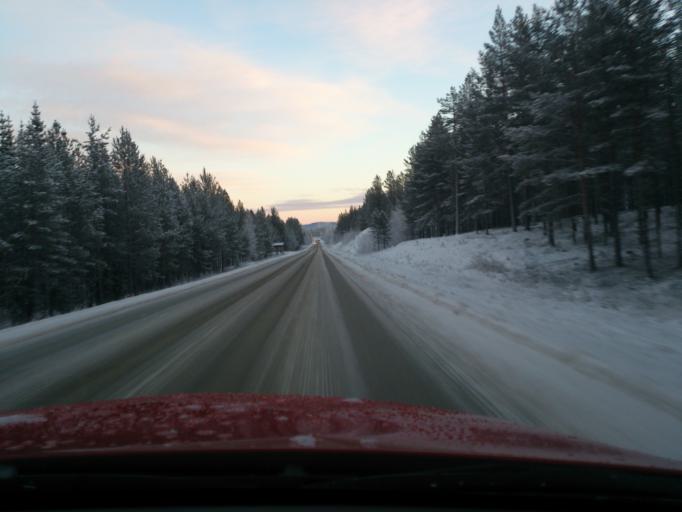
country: SE
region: Jaemtland
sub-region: Harjedalens Kommun
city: Sveg
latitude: 62.4141
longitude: 13.5626
